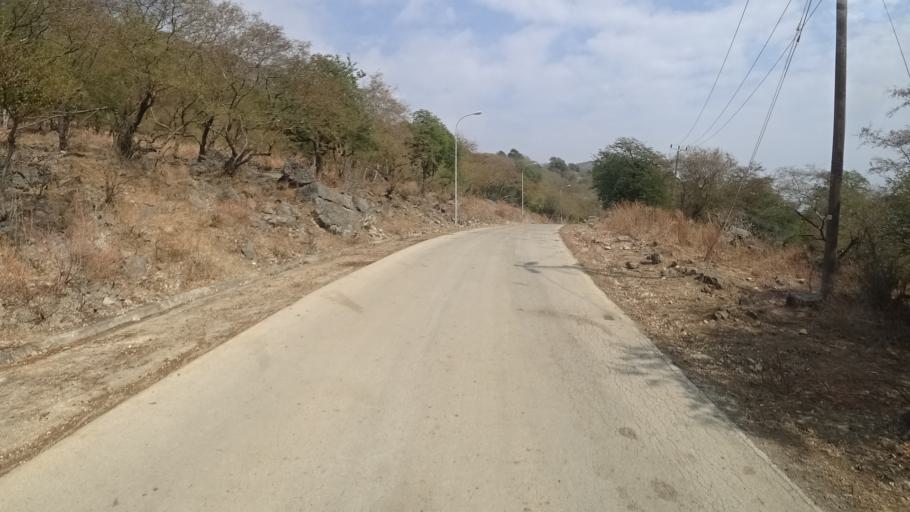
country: YE
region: Al Mahrah
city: Hawf
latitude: 16.7189
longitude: 53.2569
